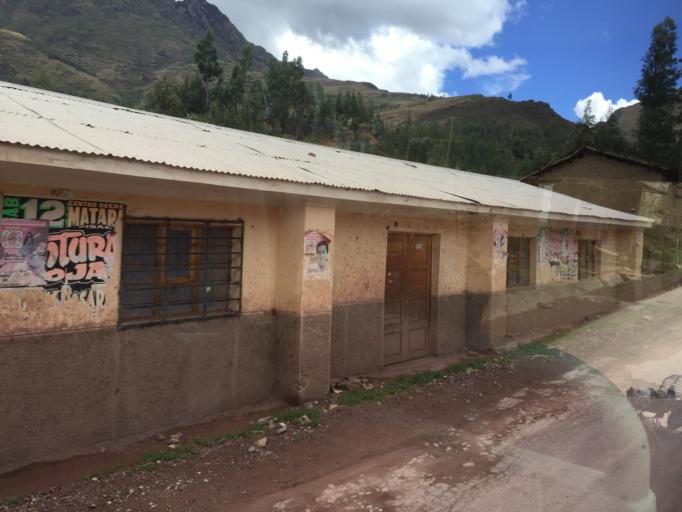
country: PE
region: Cusco
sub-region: Provincia de Calca
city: Pisac
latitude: -13.4089
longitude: -71.8342
